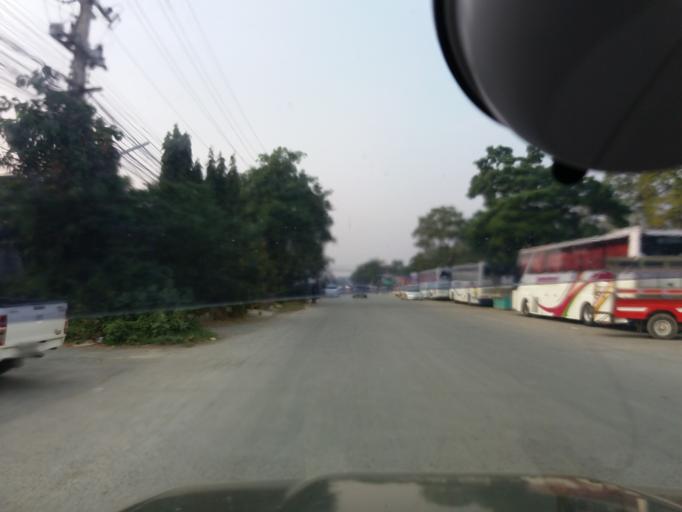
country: TH
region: Sing Buri
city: Sing Buri
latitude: 14.8890
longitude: 100.3986
